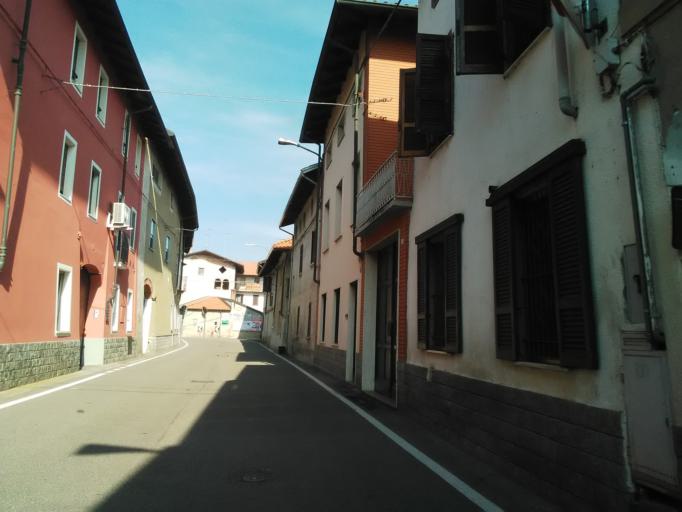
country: IT
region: Piedmont
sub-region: Provincia di Vercelli
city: Lenta
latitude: 45.5539
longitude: 8.3847
